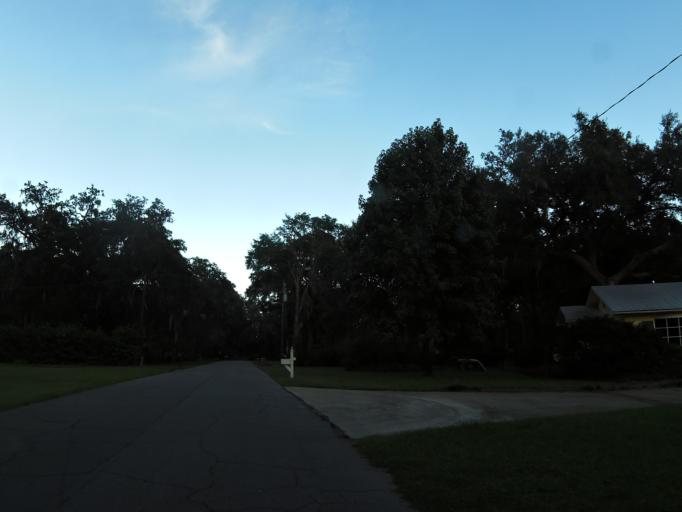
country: US
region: Georgia
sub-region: Camden County
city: St. Marys
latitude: 30.7245
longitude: -81.5584
